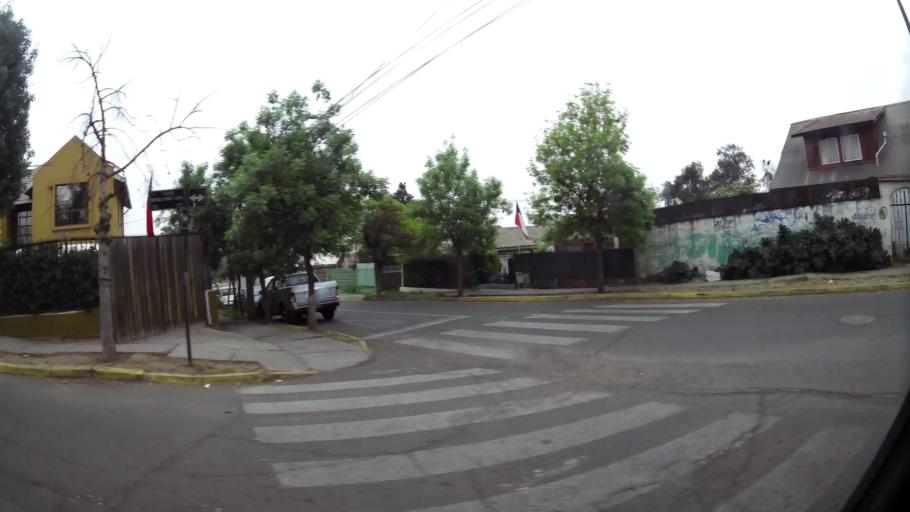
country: CL
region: Santiago Metropolitan
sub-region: Provincia de Santiago
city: Lo Prado
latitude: -33.5017
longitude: -70.7441
